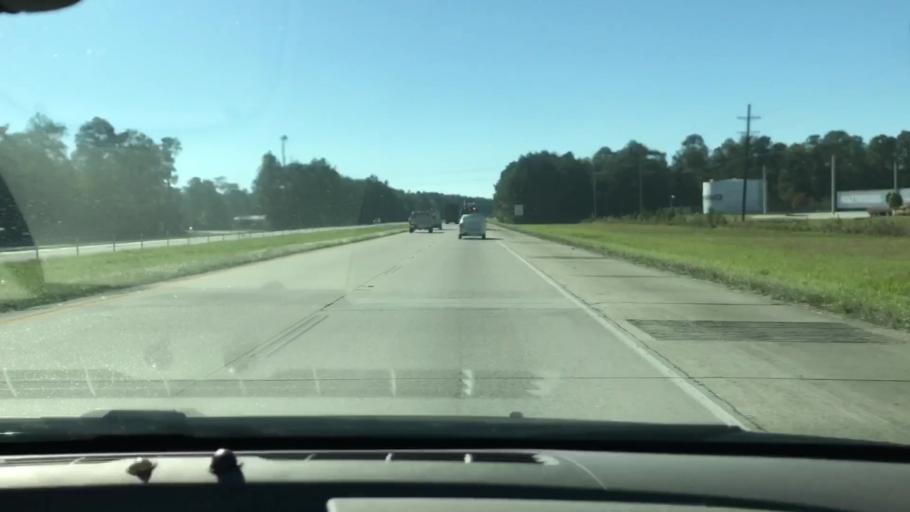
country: US
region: Louisiana
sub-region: Saint Tammany Parish
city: Pearl River
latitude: 30.3455
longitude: -89.7393
